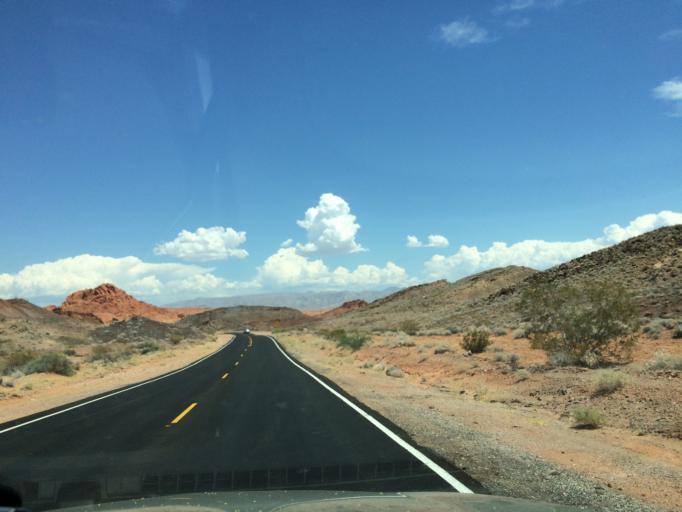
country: US
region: Nevada
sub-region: Clark County
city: Moapa Valley
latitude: 36.4267
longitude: -114.4764
